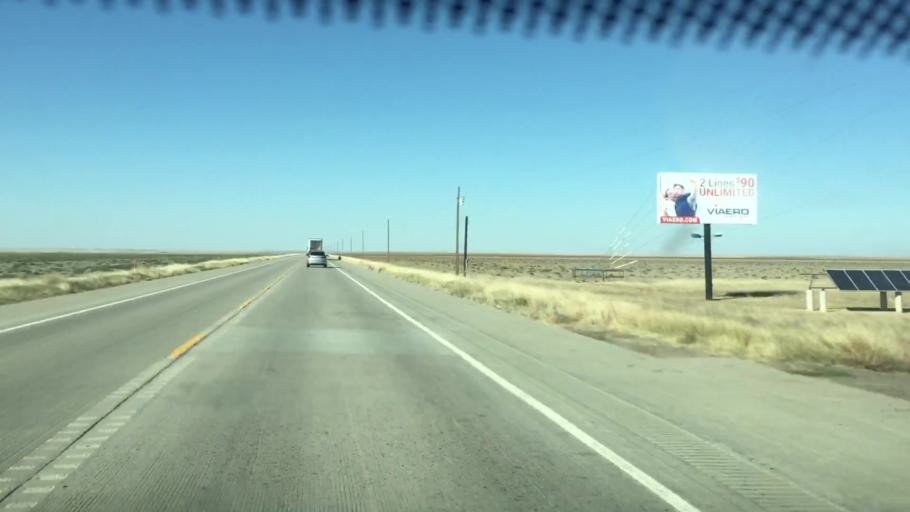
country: US
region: Colorado
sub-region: Kiowa County
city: Eads
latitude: 38.2818
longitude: -102.7199
